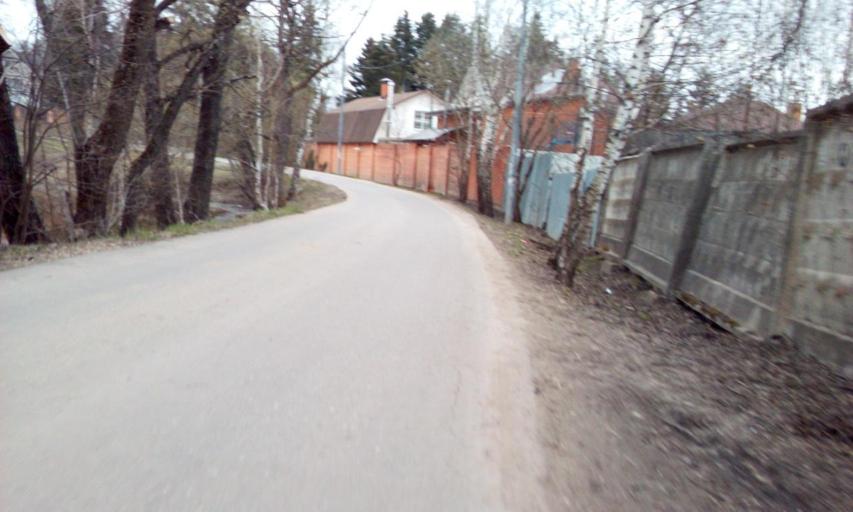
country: RU
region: Moskovskaya
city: Kokoshkino
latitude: 55.5927
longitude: 37.1737
